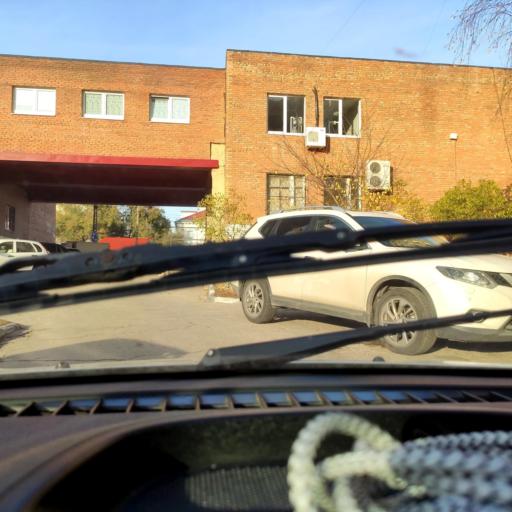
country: RU
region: Samara
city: Zhigulevsk
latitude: 53.4737
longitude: 49.4720
